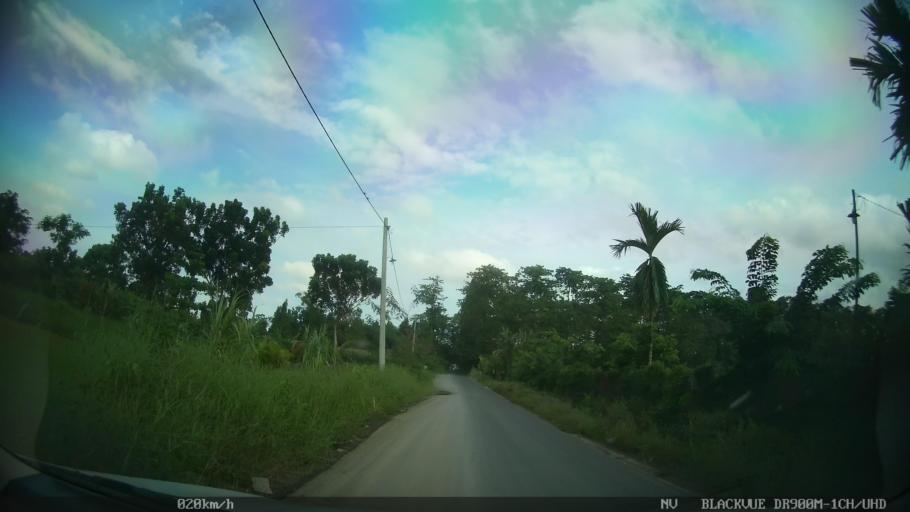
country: ID
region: North Sumatra
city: Percut
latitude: 3.5657
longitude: 98.7890
